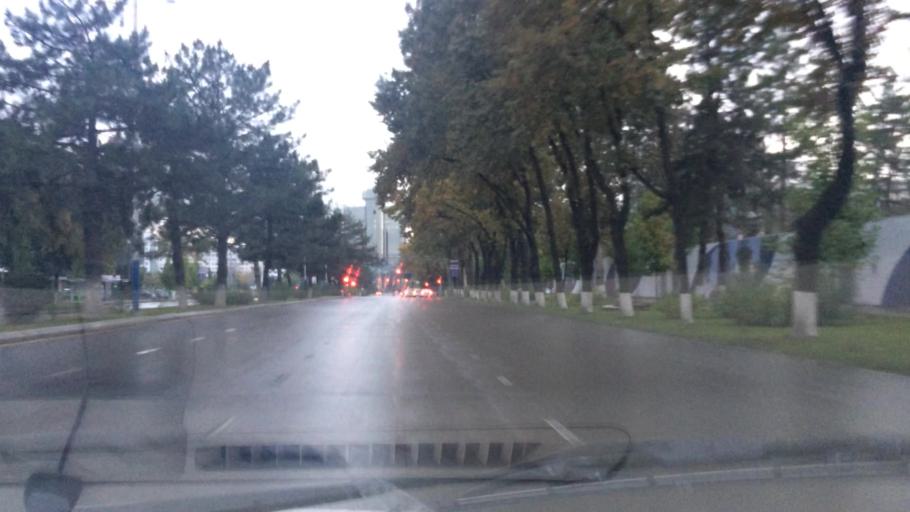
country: UZ
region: Toshkent Shahri
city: Tashkent
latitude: 41.3118
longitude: 69.2454
